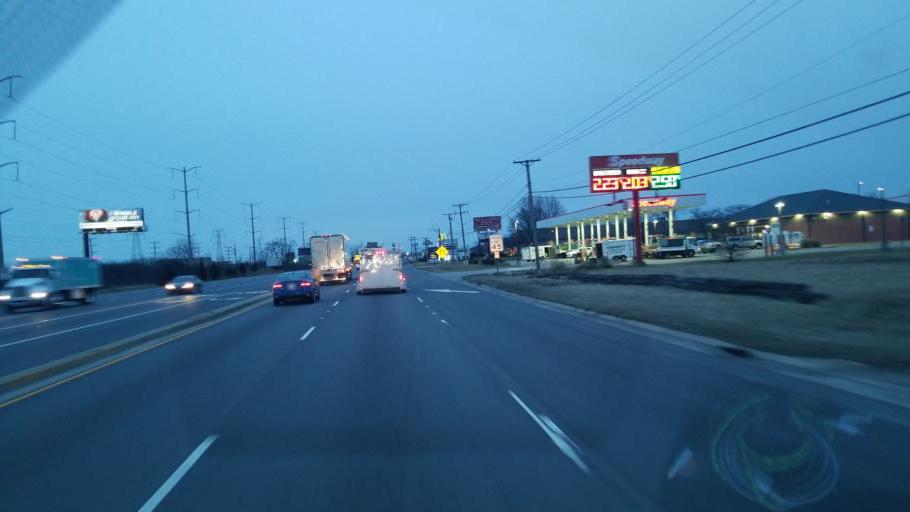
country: US
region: Illinois
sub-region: Lake County
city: Knollwood
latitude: 42.3083
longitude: -87.8769
